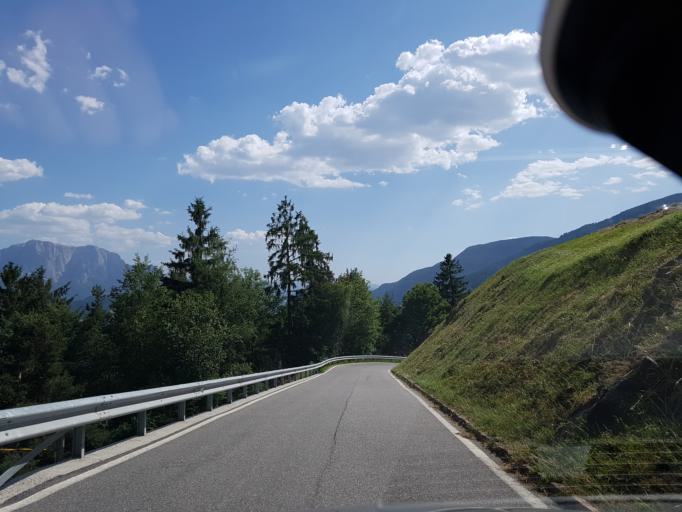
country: IT
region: Trentino-Alto Adige
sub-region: Bolzano
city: Villandro - Villanders
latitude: 46.6390
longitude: 11.5310
